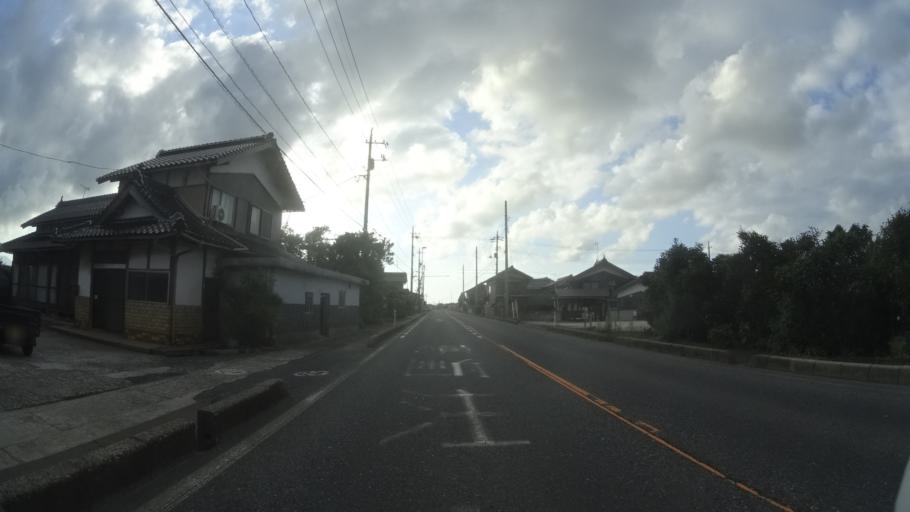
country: JP
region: Tottori
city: Kurayoshi
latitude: 35.5221
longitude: 133.5977
